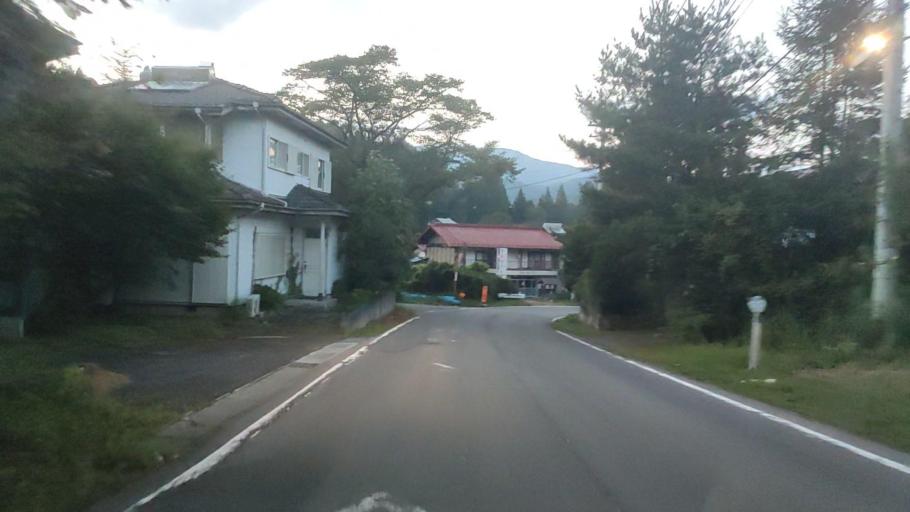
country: JP
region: Gunma
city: Nakanojomachi
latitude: 36.5427
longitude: 138.6024
